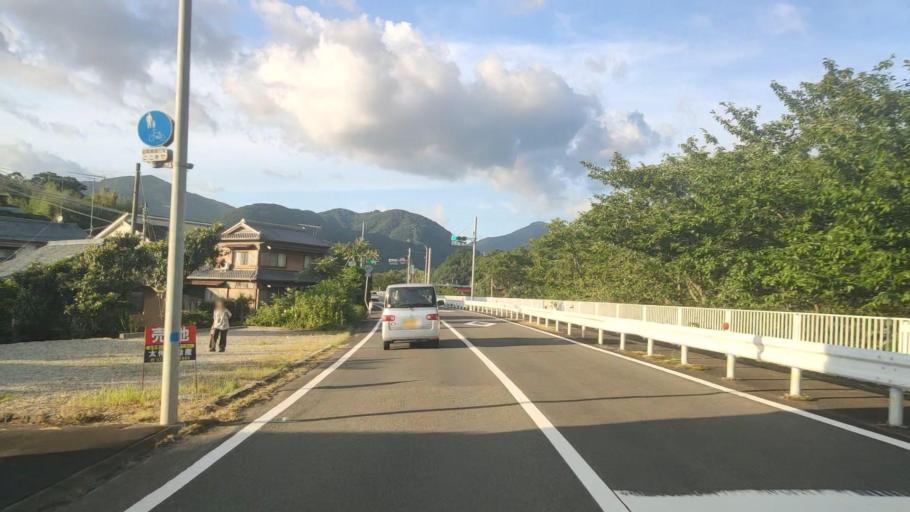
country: JP
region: Wakayama
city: Tanabe
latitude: 33.7195
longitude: 135.4810
